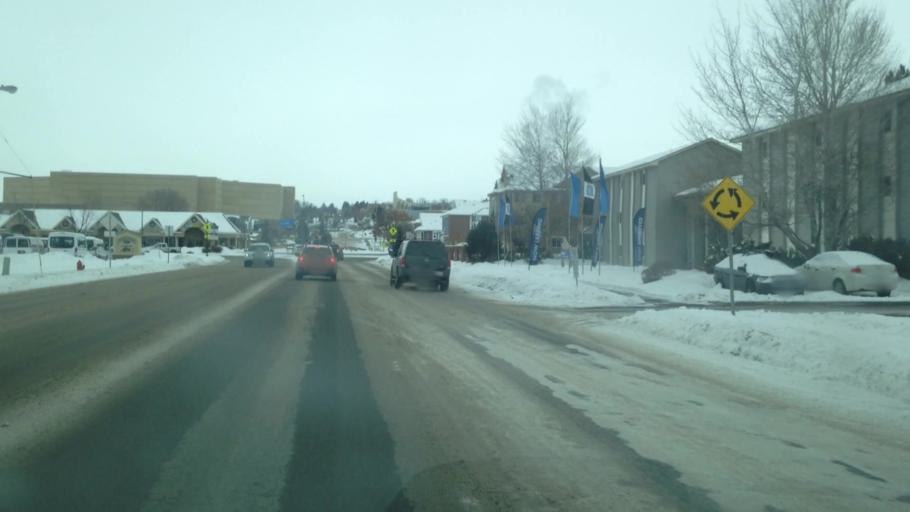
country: US
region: Idaho
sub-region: Madison County
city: Rexburg
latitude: 43.8176
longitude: -111.7915
